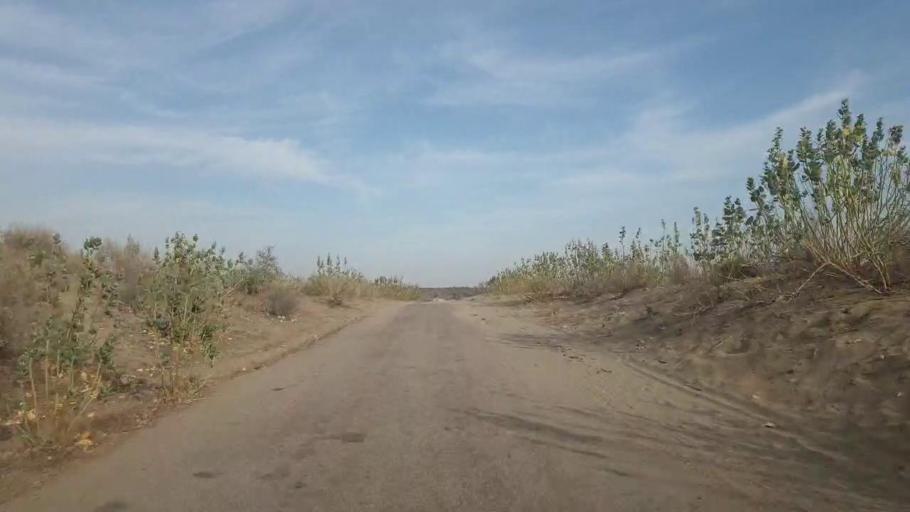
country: PK
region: Sindh
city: Nabisar
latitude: 25.0529
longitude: 69.6922
